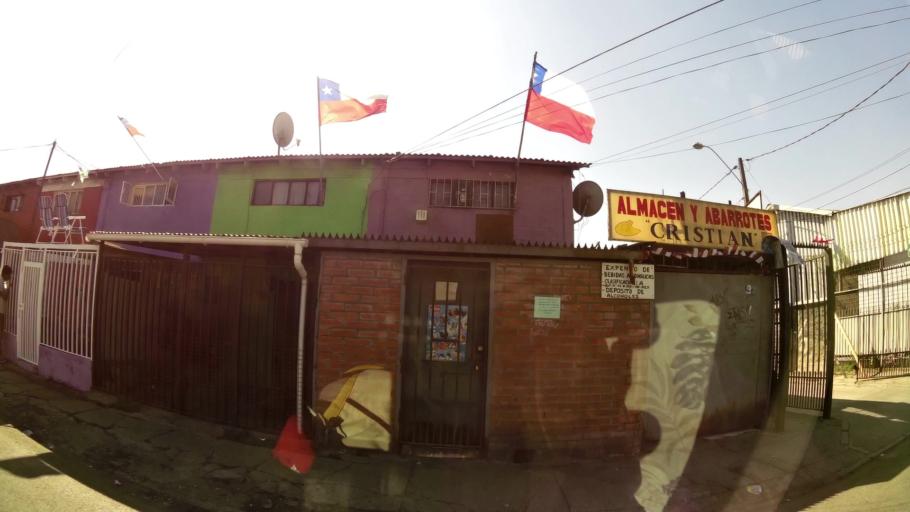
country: CL
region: Santiago Metropolitan
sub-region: Provincia de Santiago
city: La Pintana
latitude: -33.5611
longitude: -70.6224
